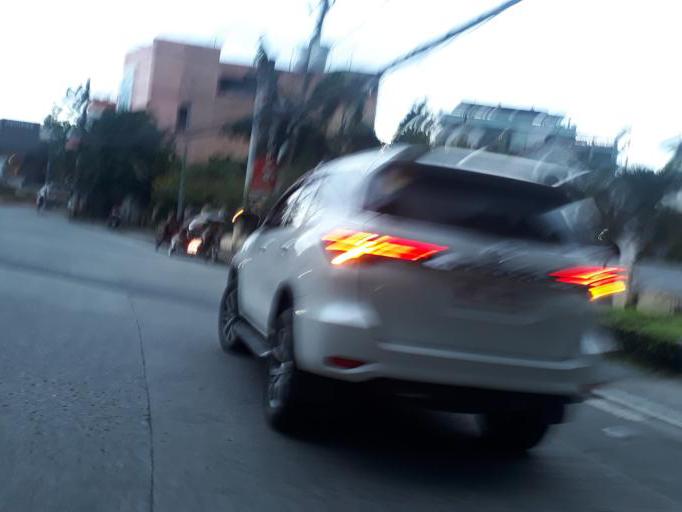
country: PH
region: Metro Manila
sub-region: Quezon City
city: Quezon City
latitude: 14.6848
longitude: 121.0773
